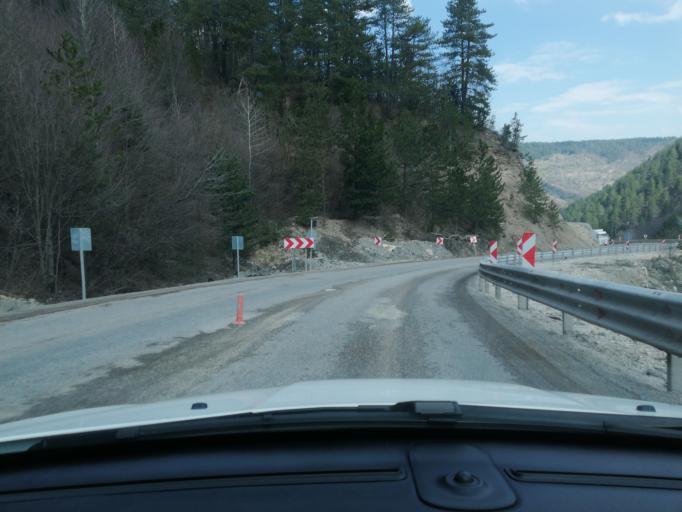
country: TR
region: Kastamonu
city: Kuzyaka
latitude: 41.1069
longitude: 33.7516
